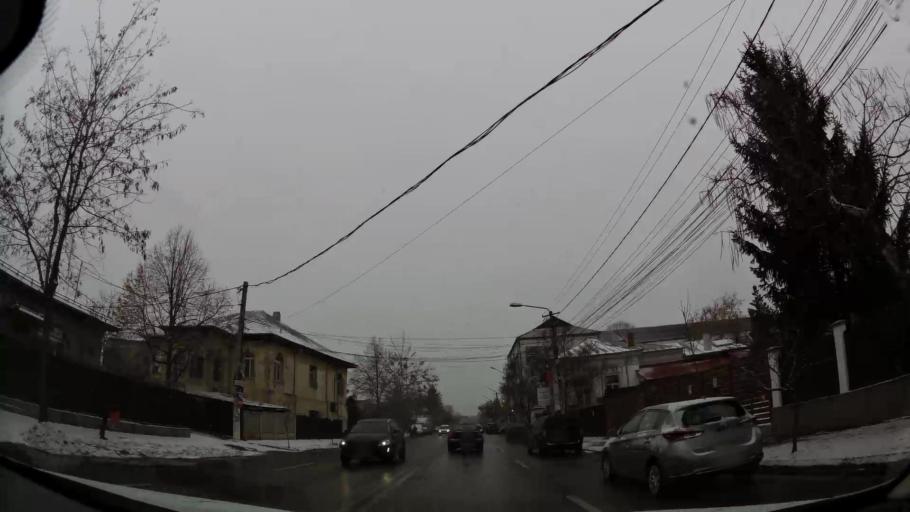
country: RO
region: Dambovita
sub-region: Municipiul Targoviste
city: Targoviste
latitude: 44.9235
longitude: 25.4723
